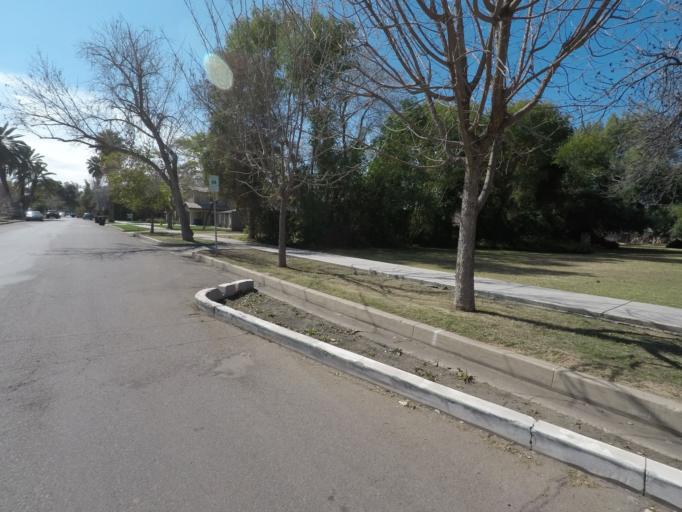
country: US
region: Arizona
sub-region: Maricopa County
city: Tempe Junction
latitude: 33.4174
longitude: -111.9425
